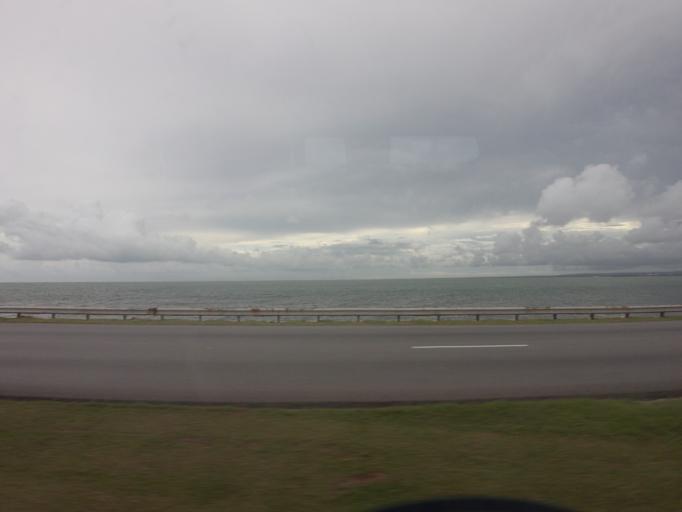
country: CU
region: Matanzas
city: Varadero
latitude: 23.1505
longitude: -81.2482
